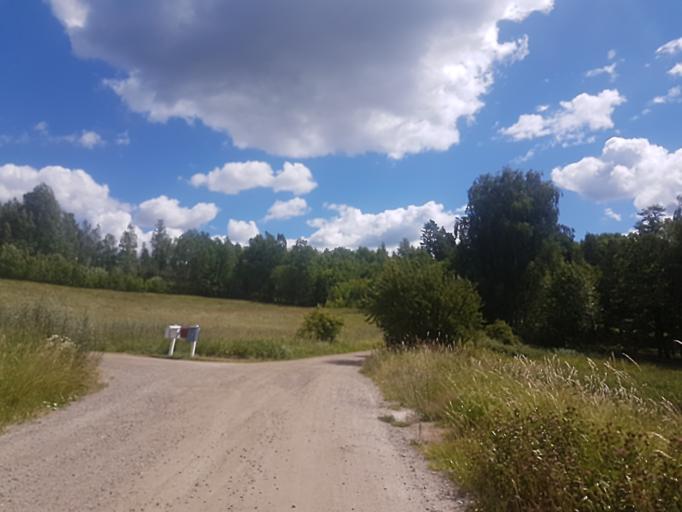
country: SE
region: Soedermanland
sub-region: Gnesta Kommun
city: Gnesta
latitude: 59.0334
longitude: 17.3512
